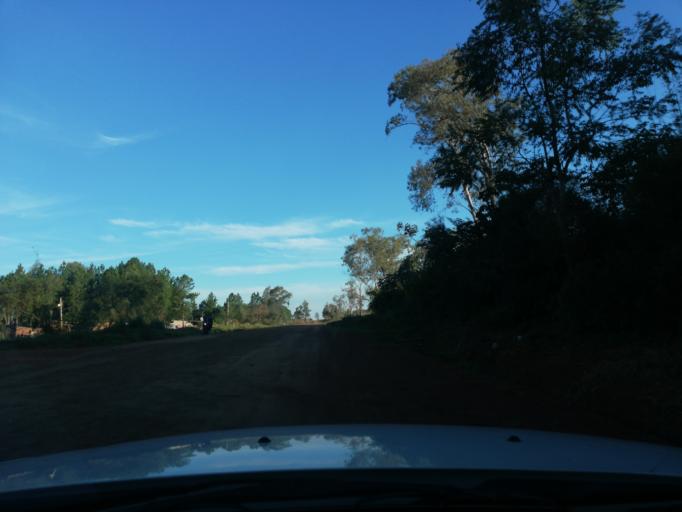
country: AR
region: Misiones
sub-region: Departamento de Capital
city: Posadas
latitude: -27.4774
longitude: -55.9709
